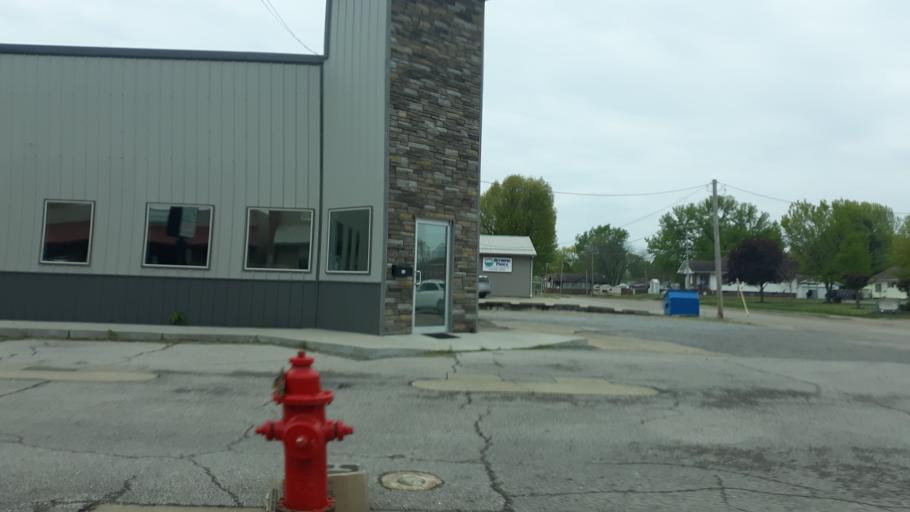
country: US
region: Illinois
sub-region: Williamson County
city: Marion
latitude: 37.7369
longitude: -88.9326
